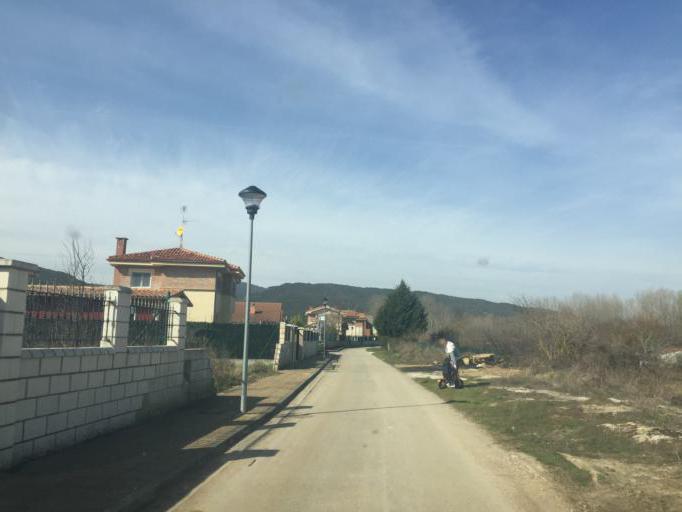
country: ES
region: Castille and Leon
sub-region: Provincia de Burgos
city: Medina de Pomar
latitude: 42.9399
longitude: -3.5859
